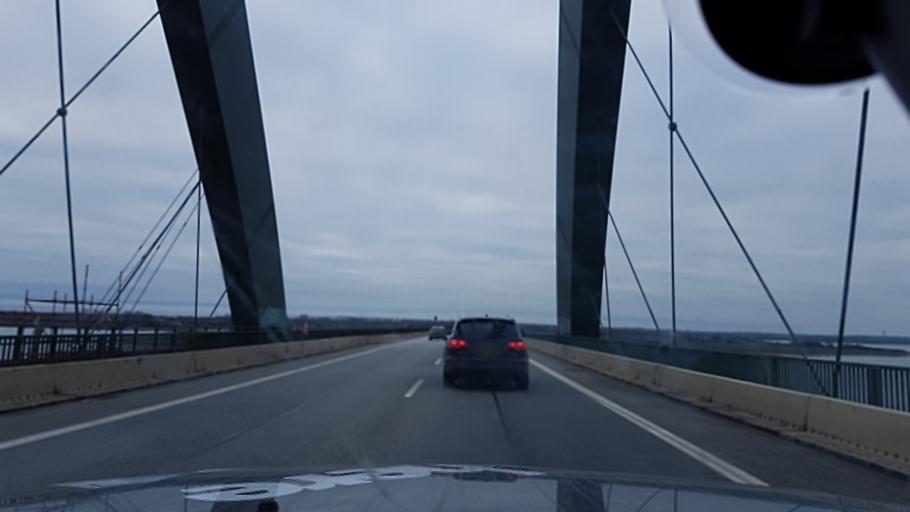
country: DE
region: Schleswig-Holstein
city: Grossenbrode
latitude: 54.4014
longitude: 11.1122
